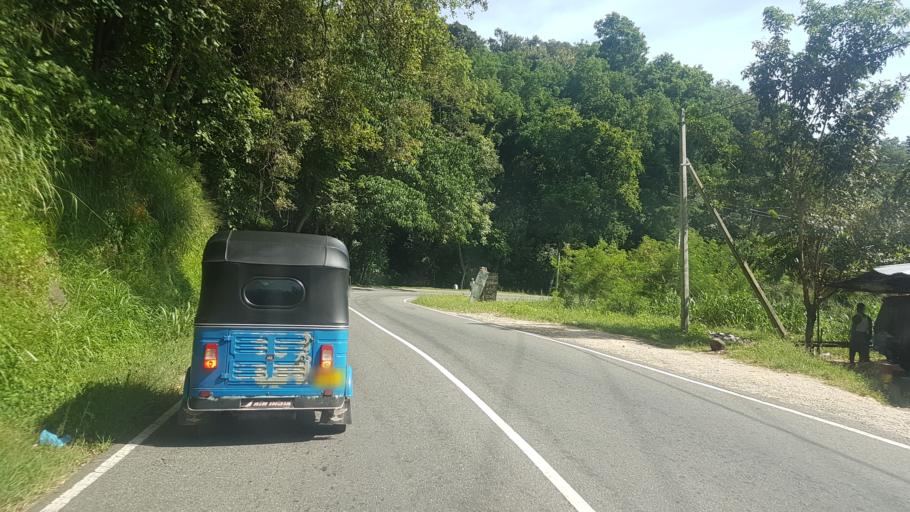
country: LK
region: Uva
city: Haputale
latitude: 6.8032
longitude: 81.0896
